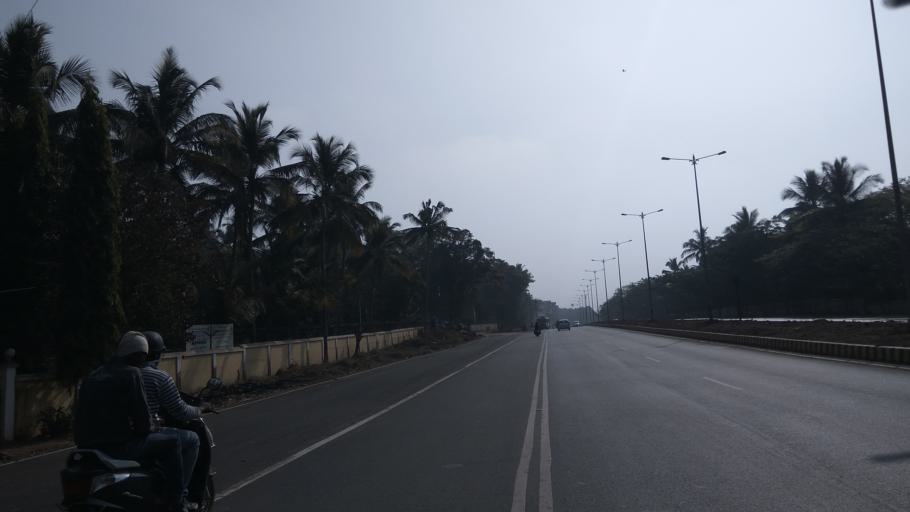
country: IN
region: Goa
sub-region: North Goa
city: Jua
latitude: 15.4994
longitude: 73.9168
